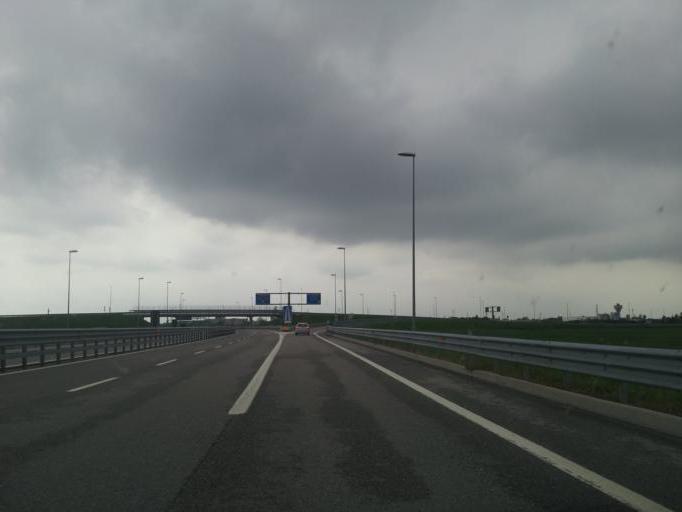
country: IT
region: Friuli Venezia Giulia
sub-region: Provincia di Udine
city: Ronchis
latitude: 45.8036
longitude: 13.0214
